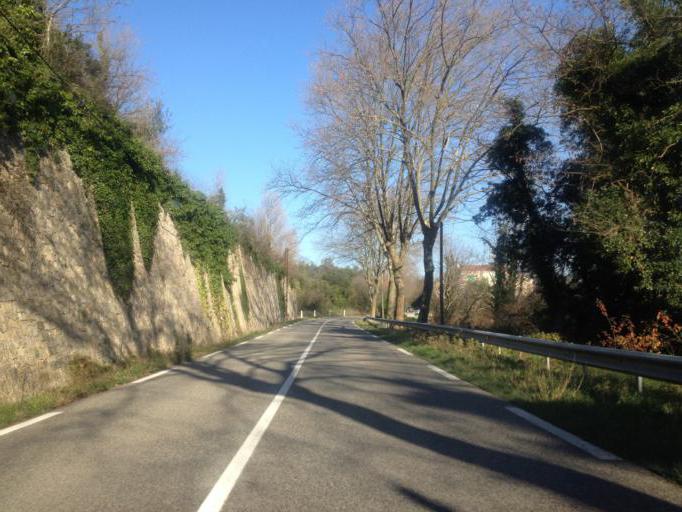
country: FR
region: Rhone-Alpes
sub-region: Departement de l'Ardeche
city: Cruas
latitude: 44.6645
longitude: 4.7662
